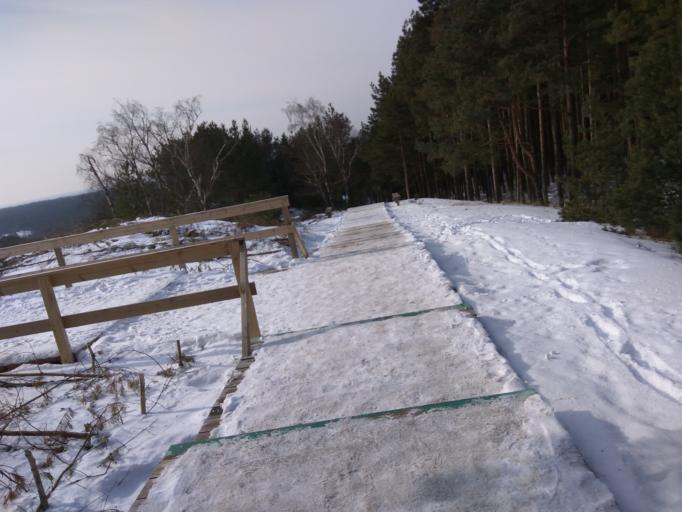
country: LT
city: Nida
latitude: 55.2211
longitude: 20.9016
